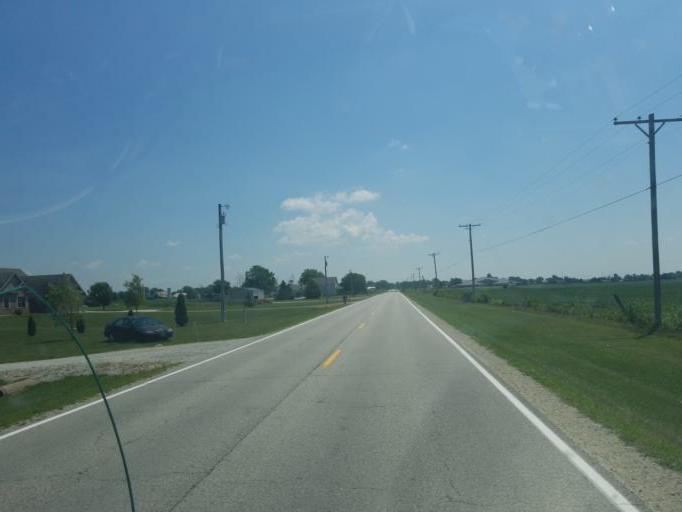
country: US
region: Ohio
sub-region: Shelby County
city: Anna
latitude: 40.4084
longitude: -84.1748
